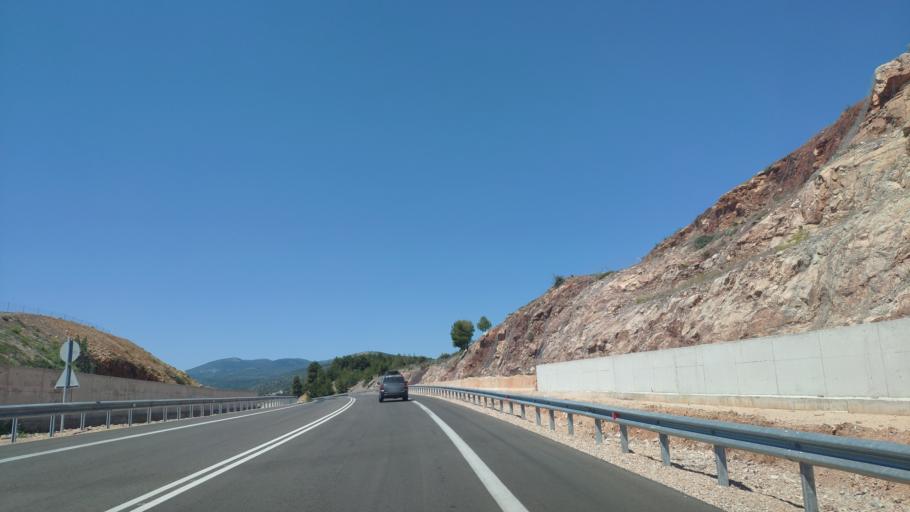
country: GR
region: Attica
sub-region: Nomarchia Dytikis Attikis
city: Mandra
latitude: 38.0810
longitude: 23.5022
